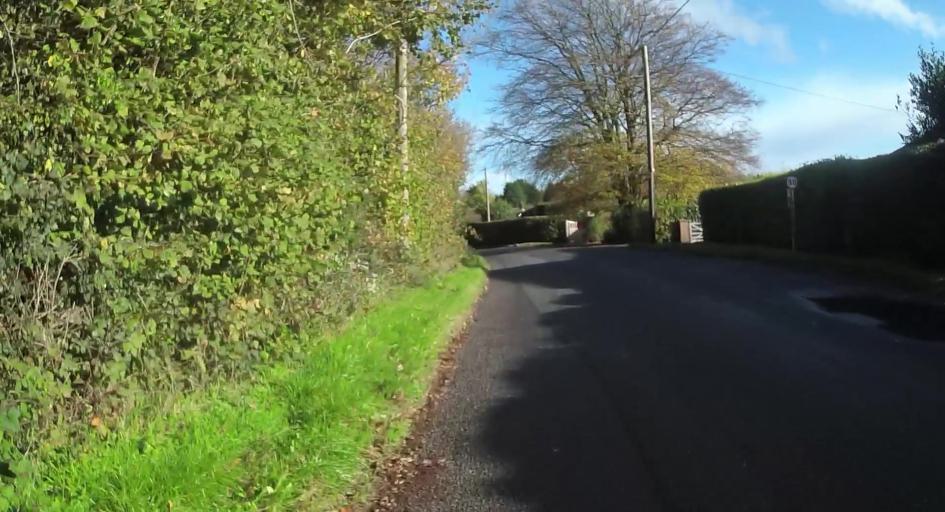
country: GB
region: England
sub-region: Hampshire
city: Four Marks
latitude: 51.1319
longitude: -1.0517
